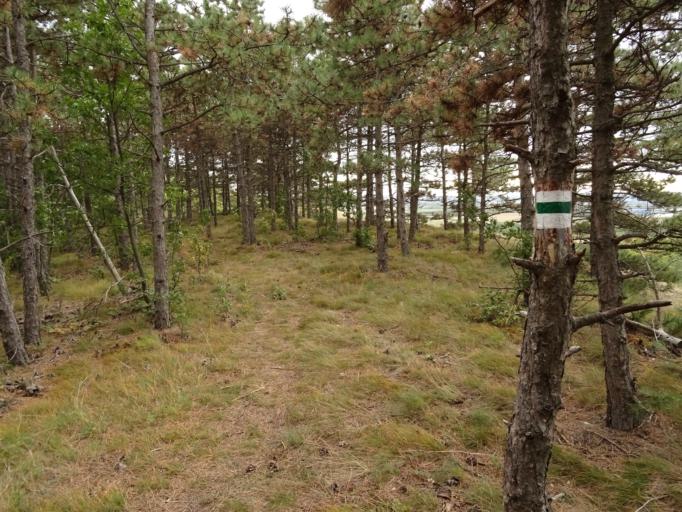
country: HU
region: Fejer
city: Kincsesbanya
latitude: 47.2166
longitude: 18.2450
